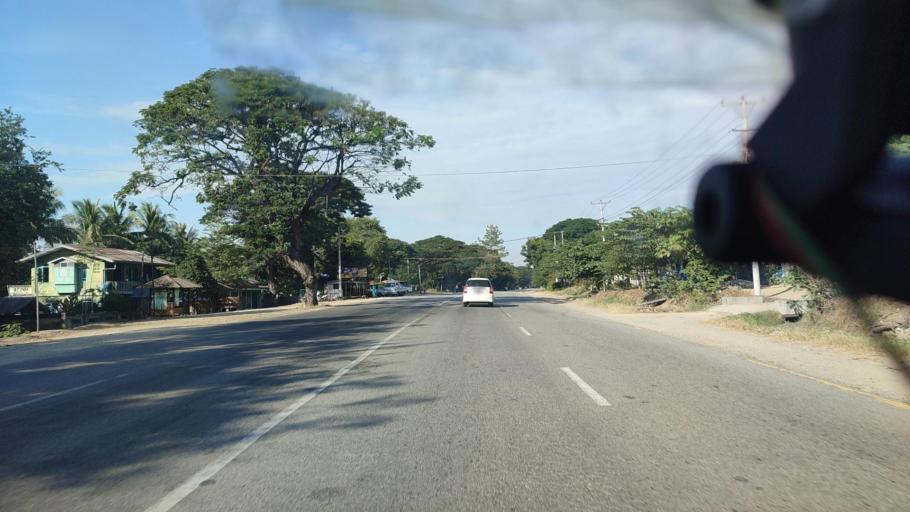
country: MM
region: Mandalay
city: Pyinmana
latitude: 20.0359
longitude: 96.2459
